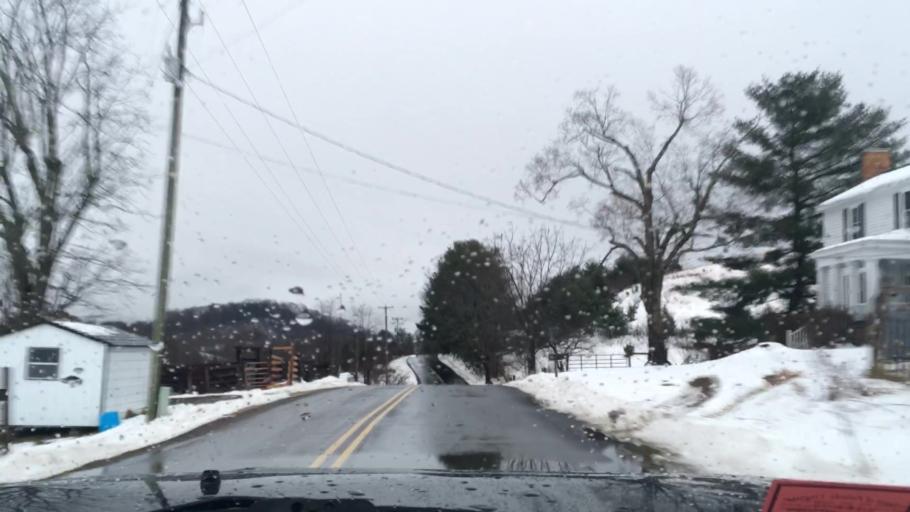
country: US
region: Virginia
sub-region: Pulaski County
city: Dublin
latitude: 37.0176
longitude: -80.6368
